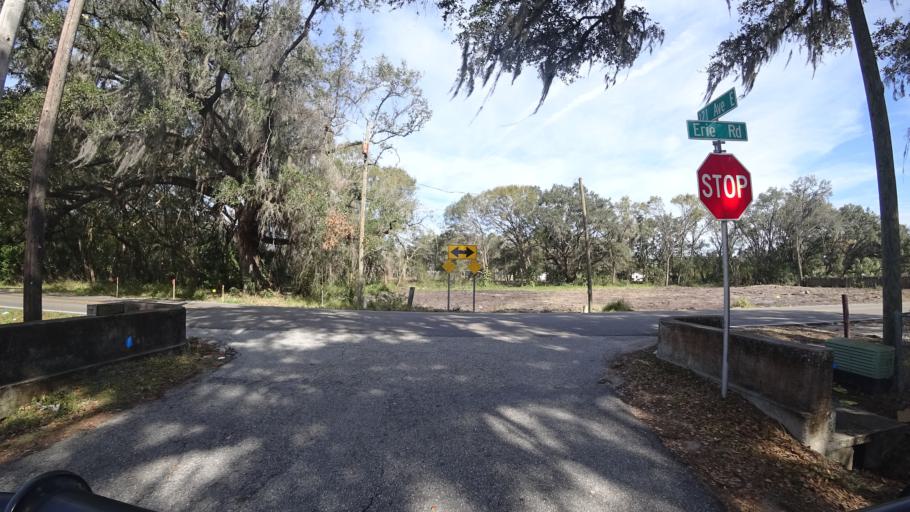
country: US
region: Florida
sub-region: Manatee County
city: Ellenton
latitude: 27.5869
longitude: -82.4277
